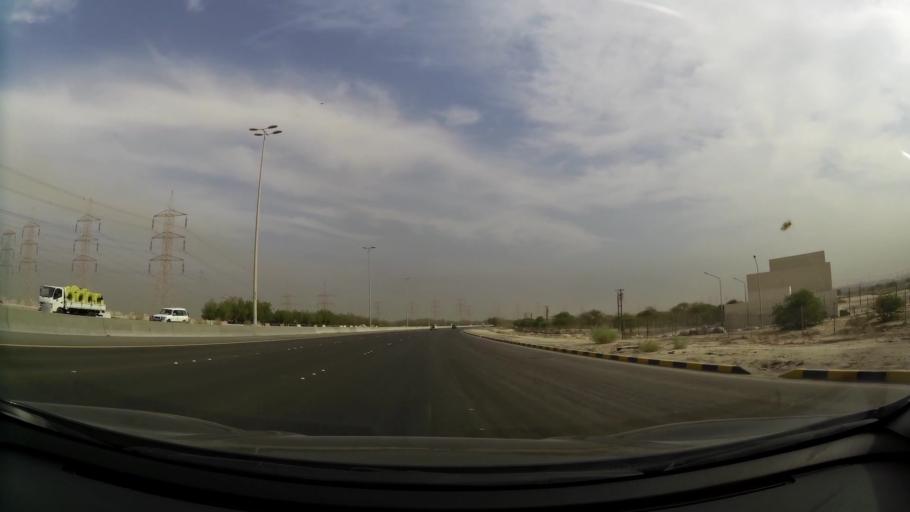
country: KW
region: Muhafazat al Jahra'
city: Al Jahra'
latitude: 29.3247
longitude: 47.7861
